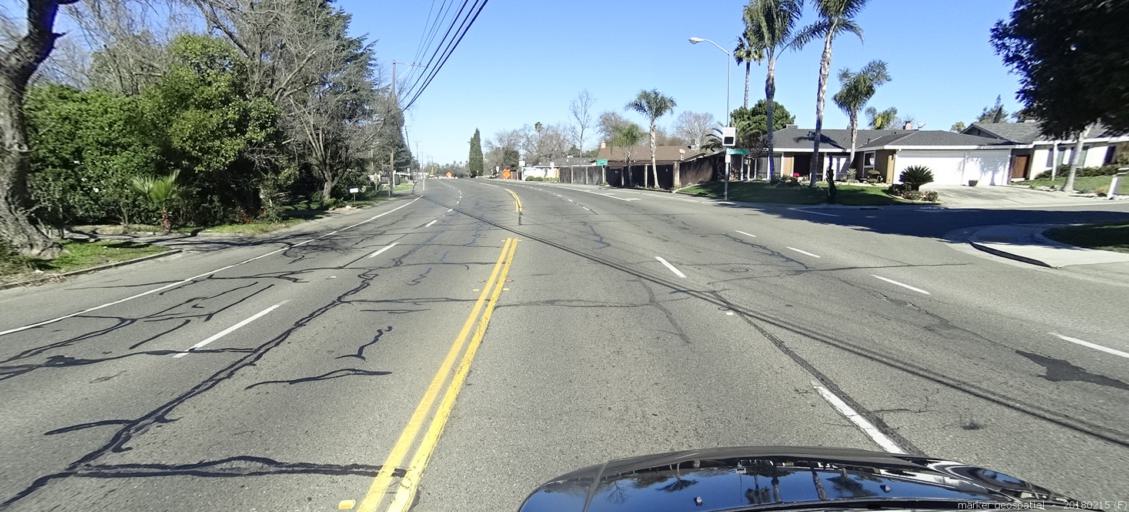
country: US
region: California
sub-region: Sacramento County
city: Antelope
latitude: 38.6709
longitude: -121.3087
